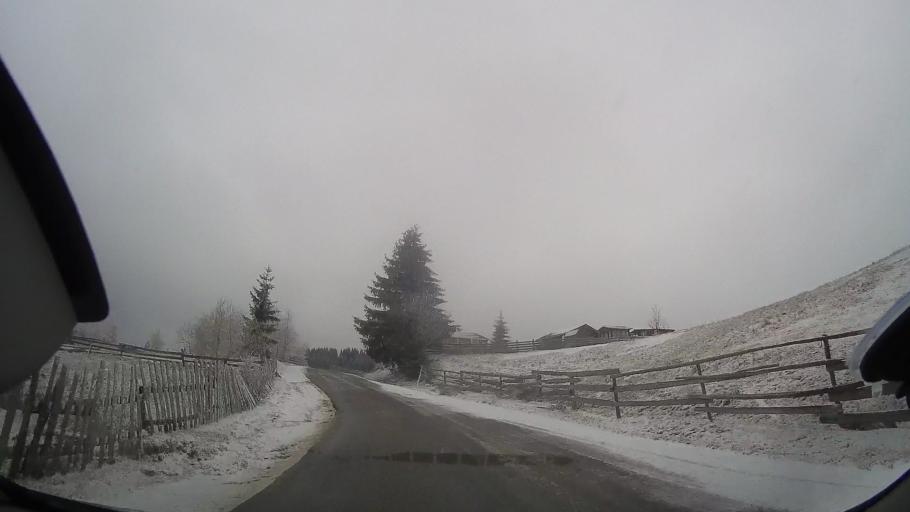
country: RO
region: Cluj
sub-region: Comuna Marisel
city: Marisel
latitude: 46.6611
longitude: 23.1074
